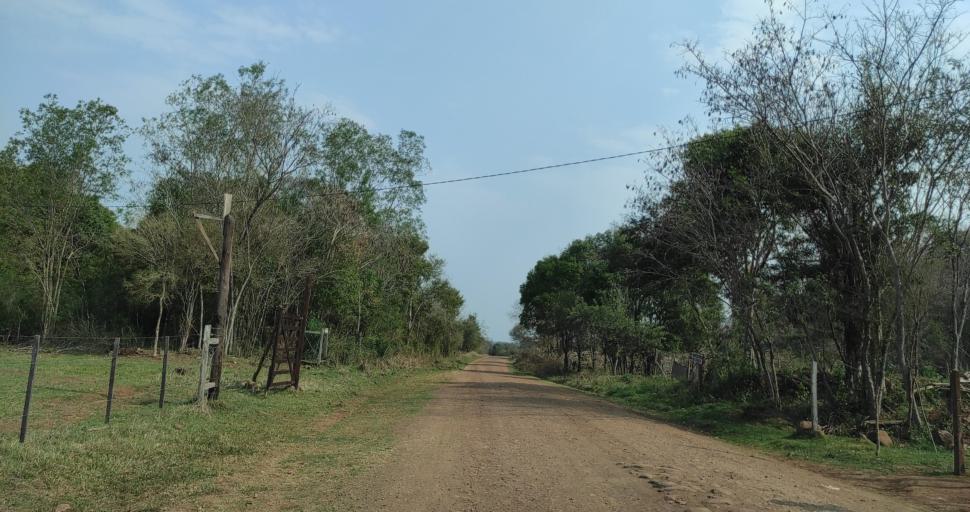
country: AR
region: Misiones
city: Cerro Cora
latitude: -27.5584
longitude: -55.5802
